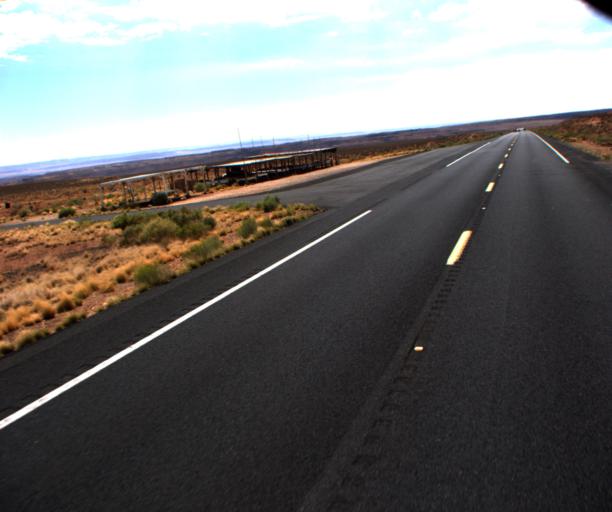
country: US
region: Arizona
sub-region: Coconino County
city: Tuba City
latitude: 35.9046
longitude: -111.5480
